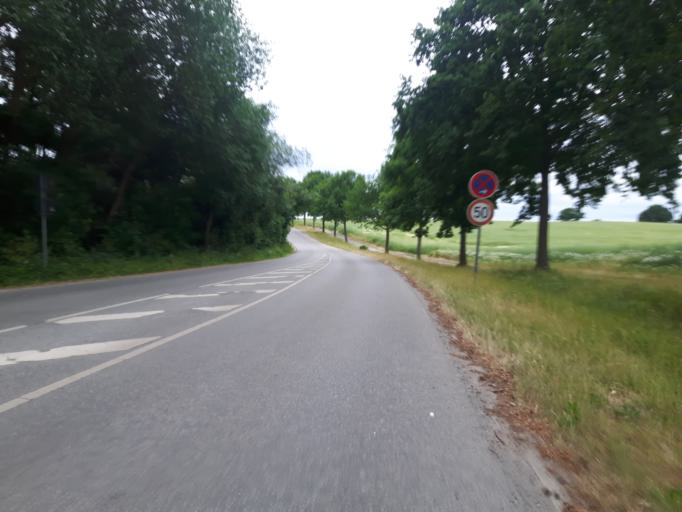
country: DE
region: Schleswig-Holstein
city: Schashagen
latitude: 54.1080
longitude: 10.8981
